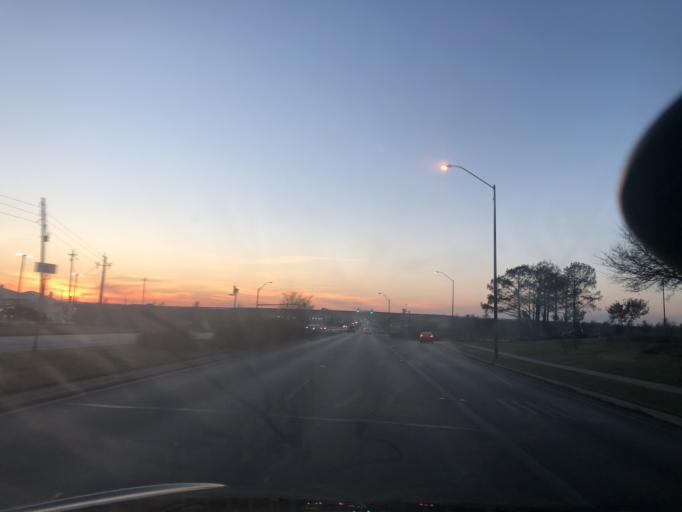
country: US
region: Texas
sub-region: Tarrant County
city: White Settlement
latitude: 32.7245
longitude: -97.4777
